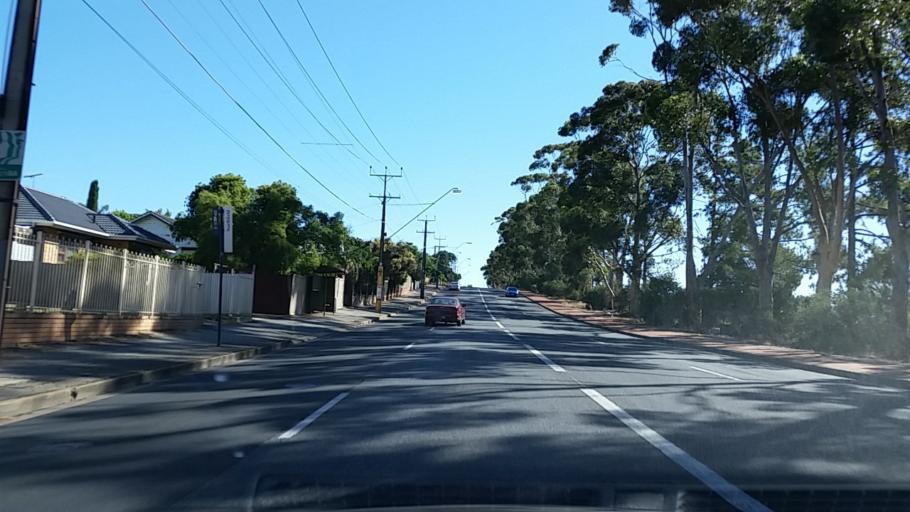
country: AU
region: South Australia
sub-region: Salisbury
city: Ingle Farm
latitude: -34.8389
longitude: 138.6234
